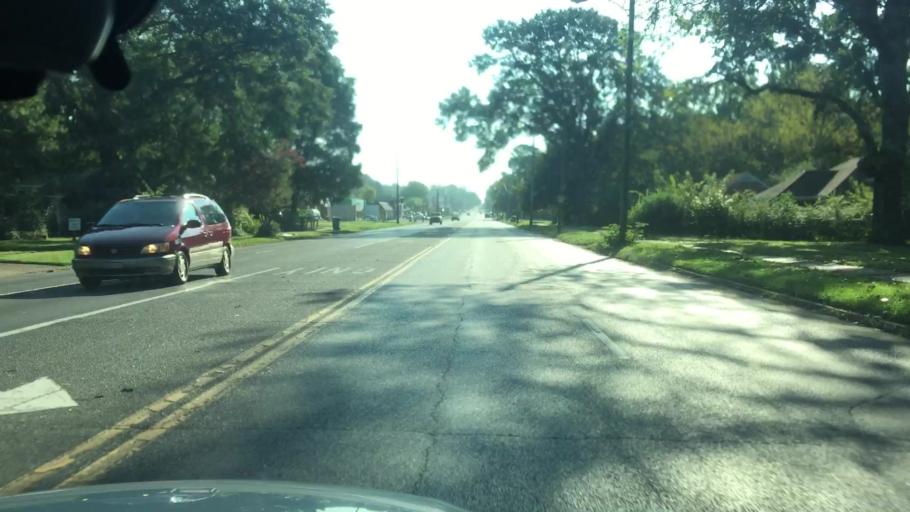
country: US
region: Tennessee
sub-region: Shelby County
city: Bartlett
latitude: 35.1076
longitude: -89.9382
